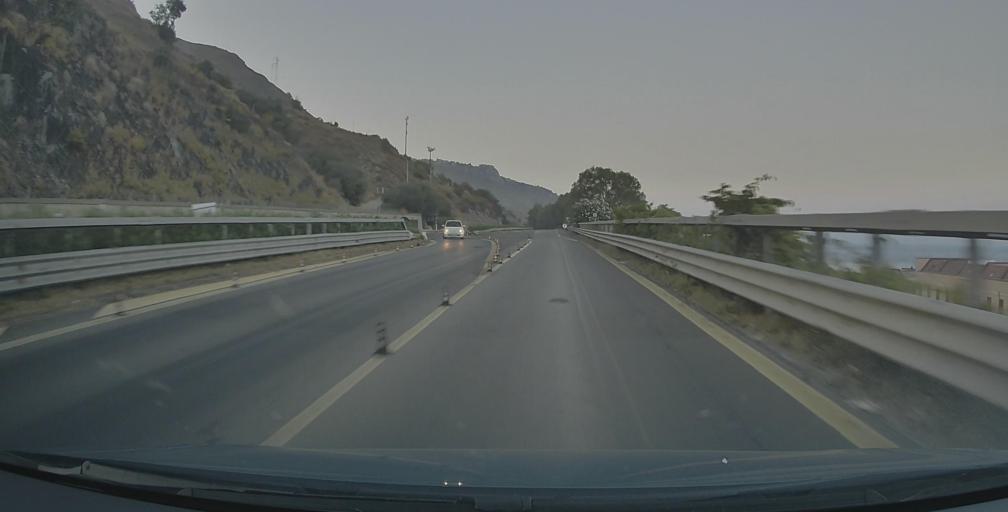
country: IT
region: Sicily
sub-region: Messina
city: Letojanni
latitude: 37.8932
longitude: 15.3206
